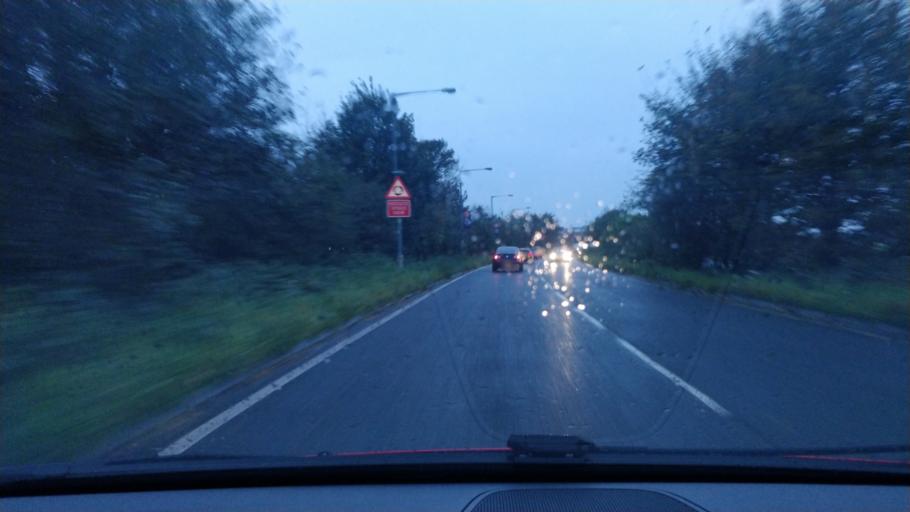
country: GB
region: England
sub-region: Blackpool
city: Blackpool
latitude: 53.7941
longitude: -3.0437
